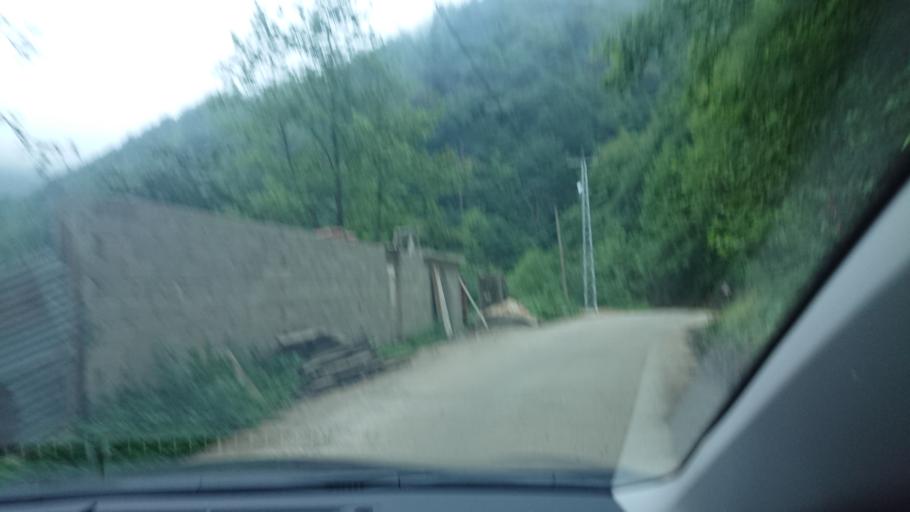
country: TR
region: Rize
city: Cayeli
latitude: 41.0472
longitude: 40.8004
